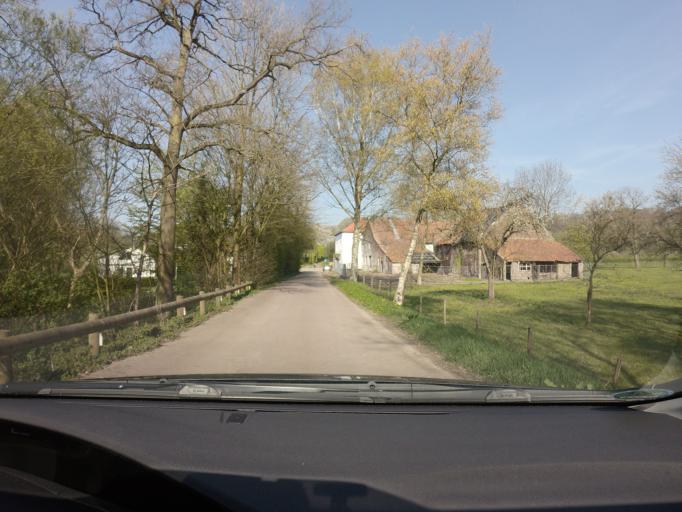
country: NL
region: Limburg
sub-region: Gemeente Meerssen
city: Meerssen
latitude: 50.8948
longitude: 5.7672
